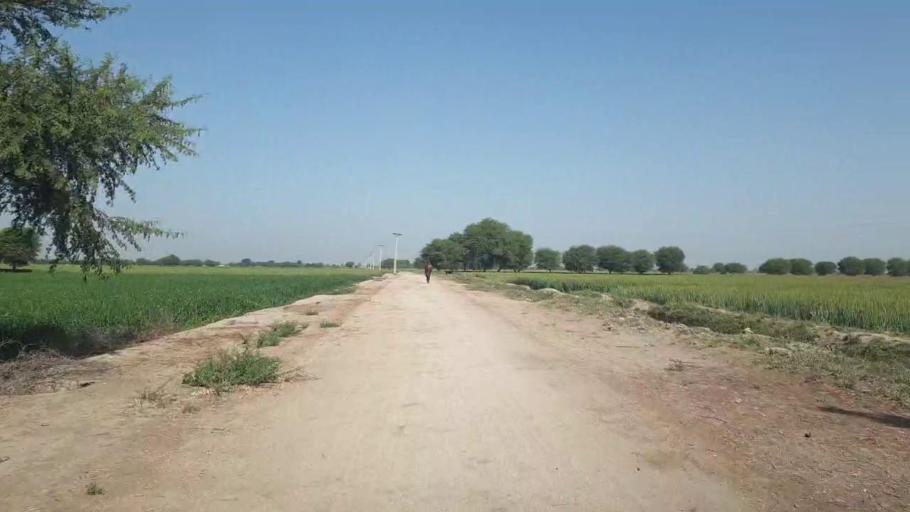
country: PK
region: Sindh
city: Umarkot
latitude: 25.3077
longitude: 69.6576
